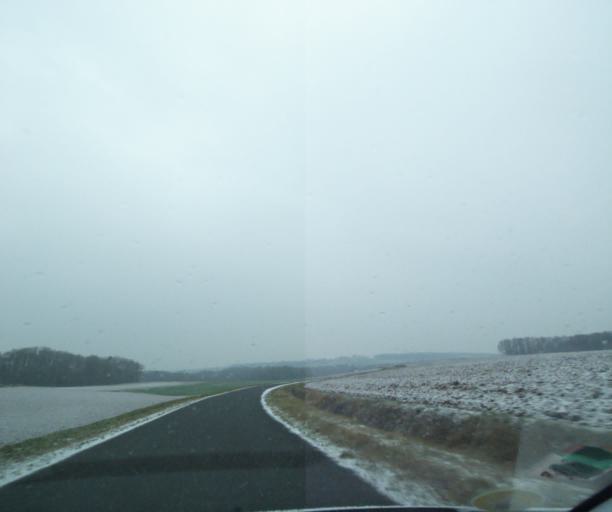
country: FR
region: Champagne-Ardenne
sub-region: Departement de la Haute-Marne
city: Chevillon
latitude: 48.4888
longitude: 5.0571
